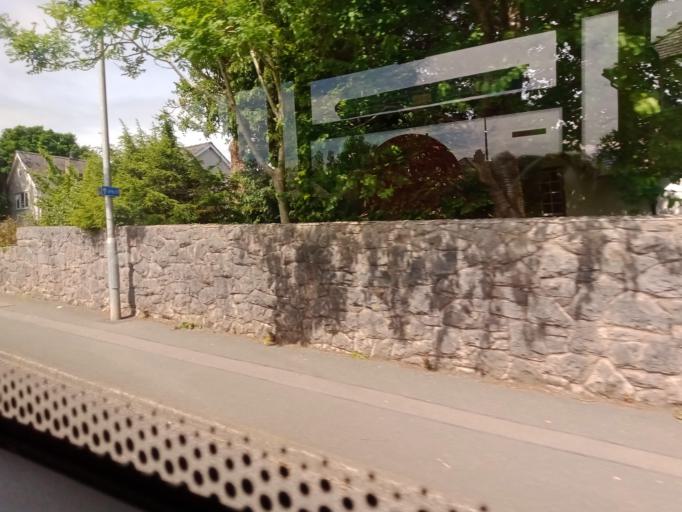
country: GB
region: Wales
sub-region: Anglesey
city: Menai Bridge
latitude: 53.2130
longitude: -4.1565
